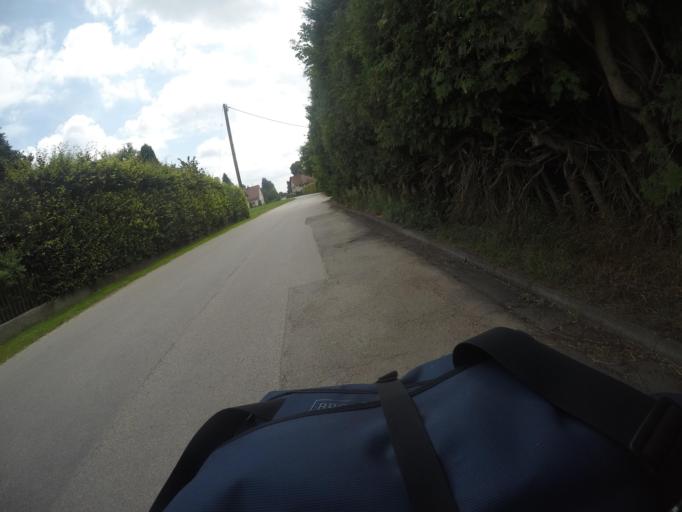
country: DE
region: Bavaria
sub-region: Swabia
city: Fellheim
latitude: 48.0929
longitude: 10.1548
